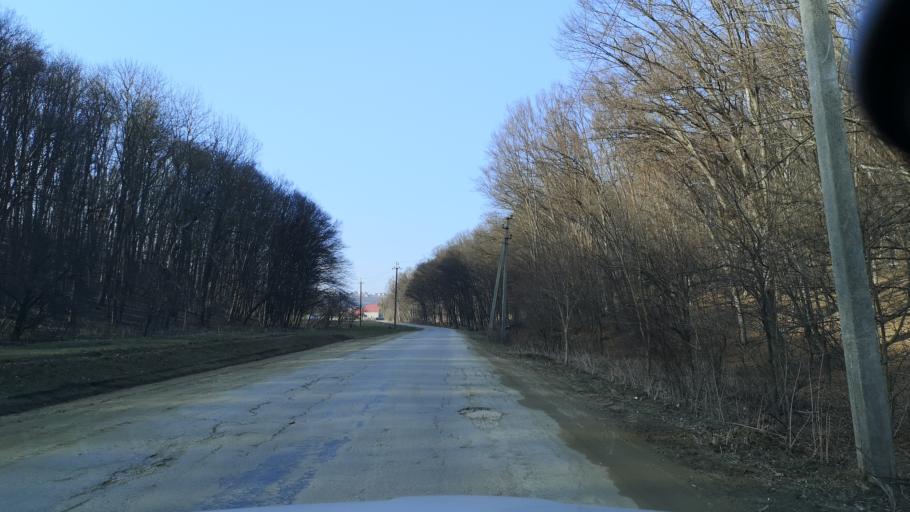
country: MD
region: Nisporeni
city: Nisporeni
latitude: 47.0853
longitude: 28.3212
